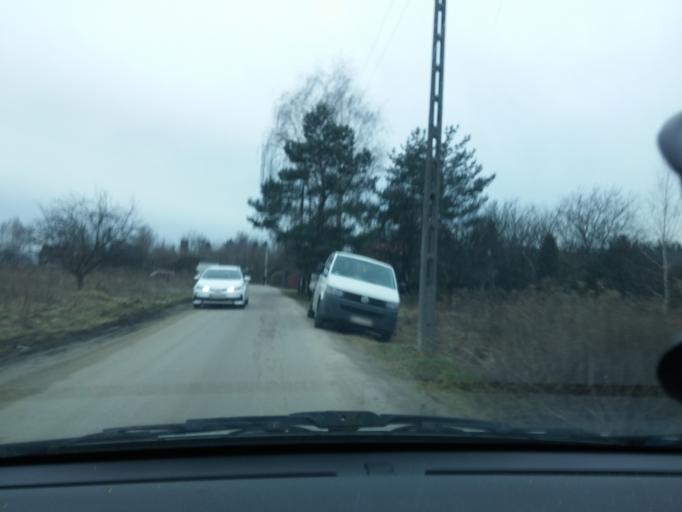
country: PL
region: Masovian Voivodeship
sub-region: Warszawa
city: Wilanow
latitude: 52.1938
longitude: 21.1267
